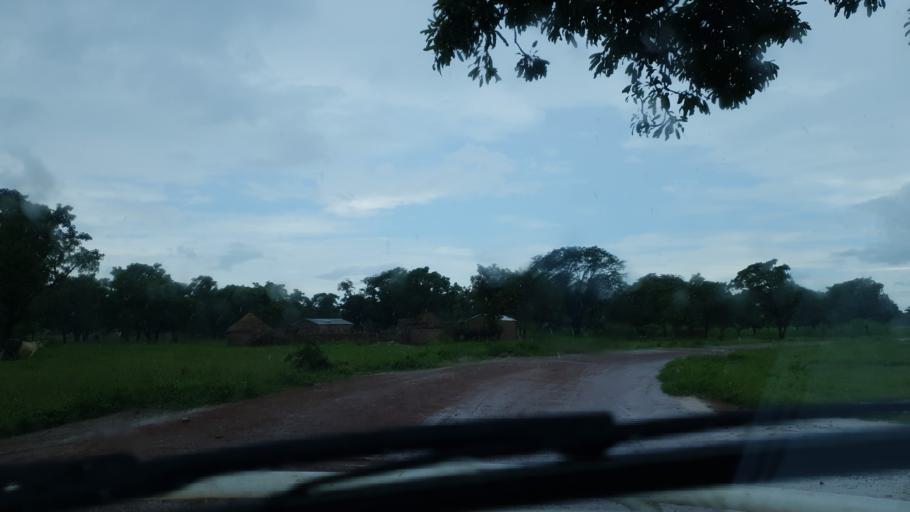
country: ML
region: Sikasso
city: Kolondieba
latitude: 11.5964
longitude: -6.6613
